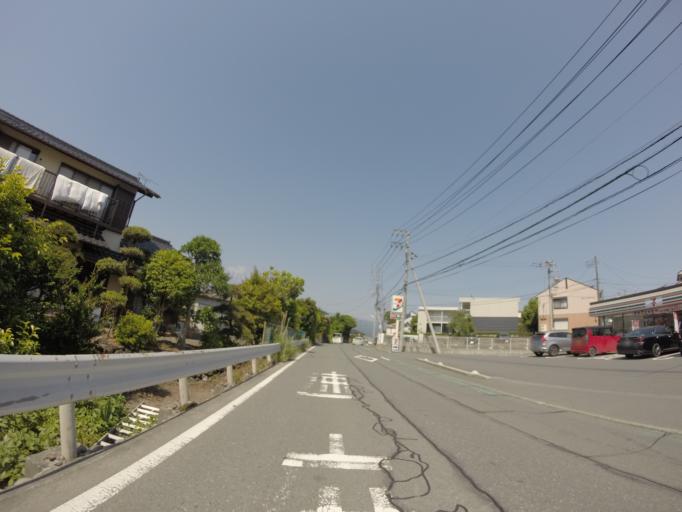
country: JP
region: Shizuoka
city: Fujinomiya
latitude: 35.2191
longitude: 138.5954
